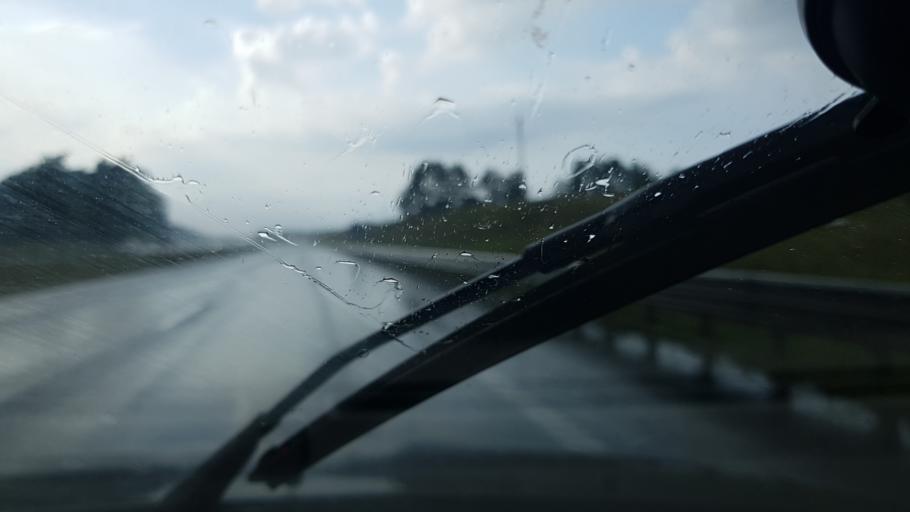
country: PL
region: Warmian-Masurian Voivodeship
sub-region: Powiat olsztynski
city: Olsztynek
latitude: 53.5110
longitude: 20.3032
